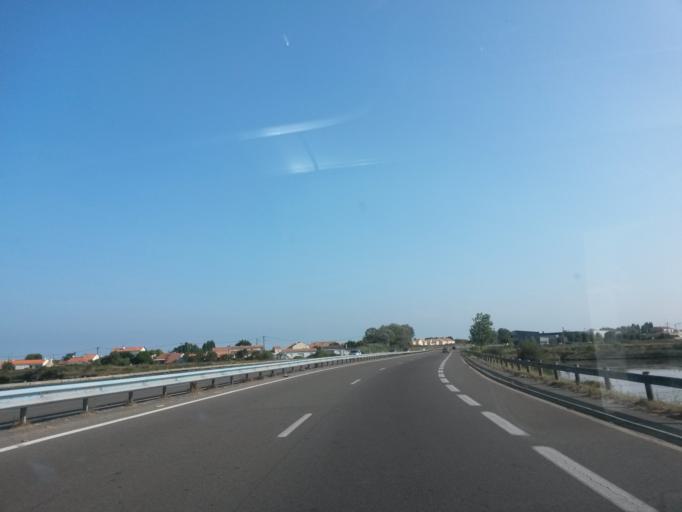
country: FR
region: Pays de la Loire
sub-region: Departement de la Vendee
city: Les Sables-d'Olonne
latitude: 46.5104
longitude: -1.7934
